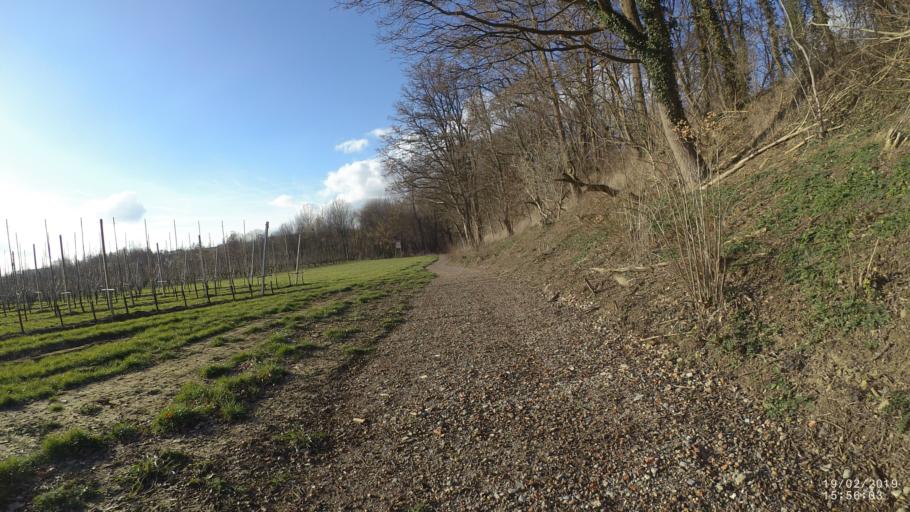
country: BE
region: Flanders
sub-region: Provincie Limburg
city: Borgloon
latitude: 50.8135
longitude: 5.3871
